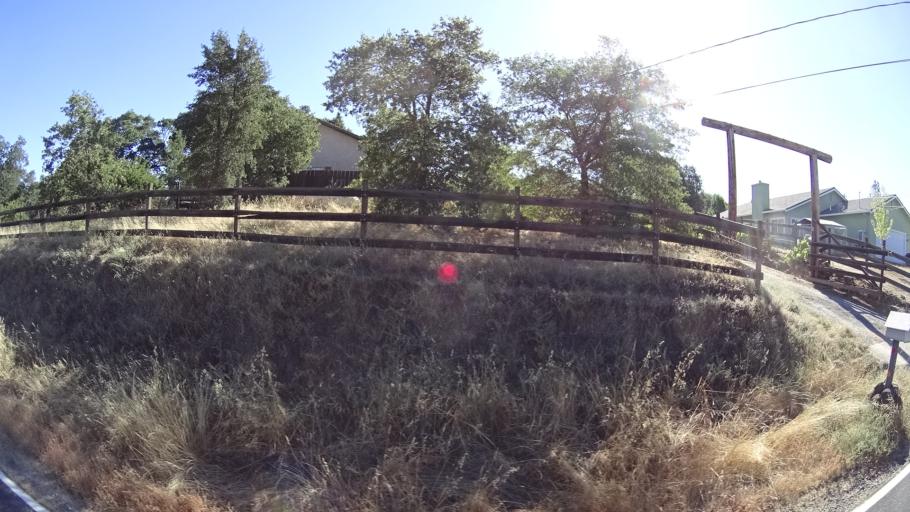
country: US
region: California
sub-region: Calaveras County
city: Rancho Calaveras
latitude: 38.1224
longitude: -120.8559
